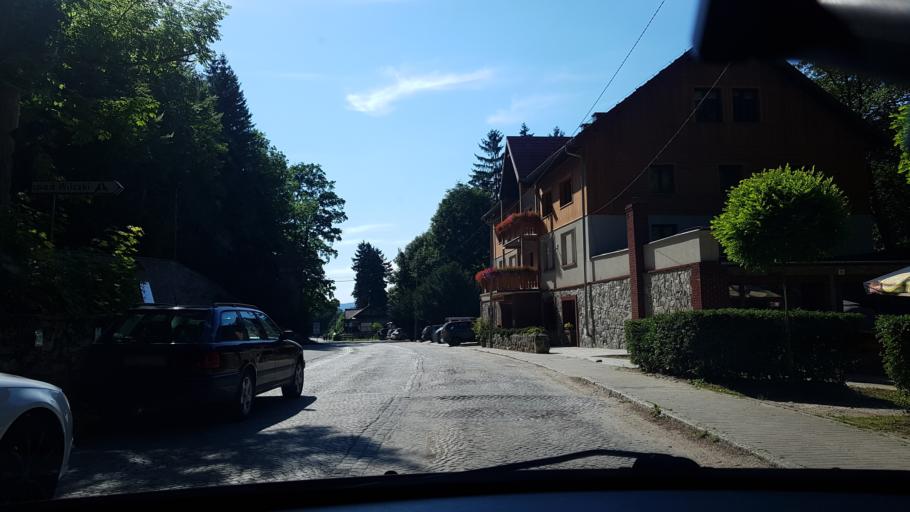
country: PL
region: Lower Silesian Voivodeship
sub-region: Powiat klodzki
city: Miedzylesie
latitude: 50.2286
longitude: 16.7605
